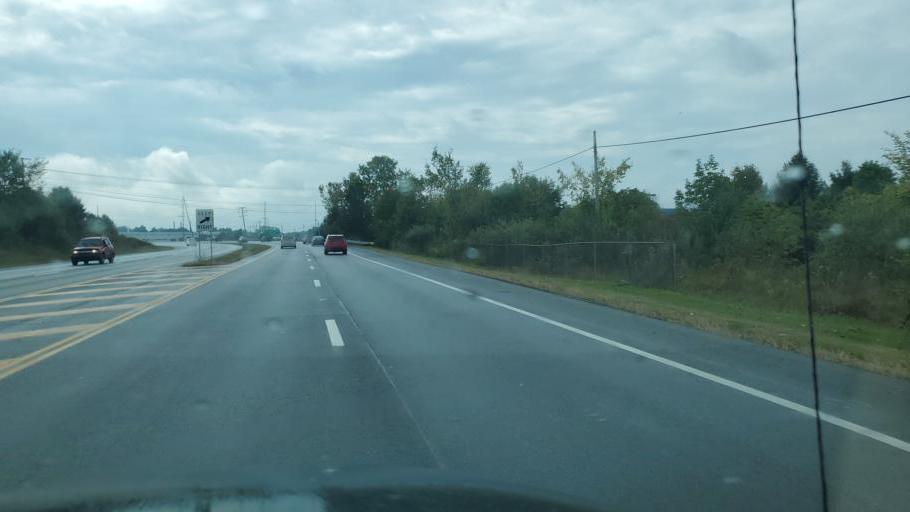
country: US
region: Ohio
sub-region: Licking County
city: Hebron
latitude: 39.9748
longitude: -82.4878
